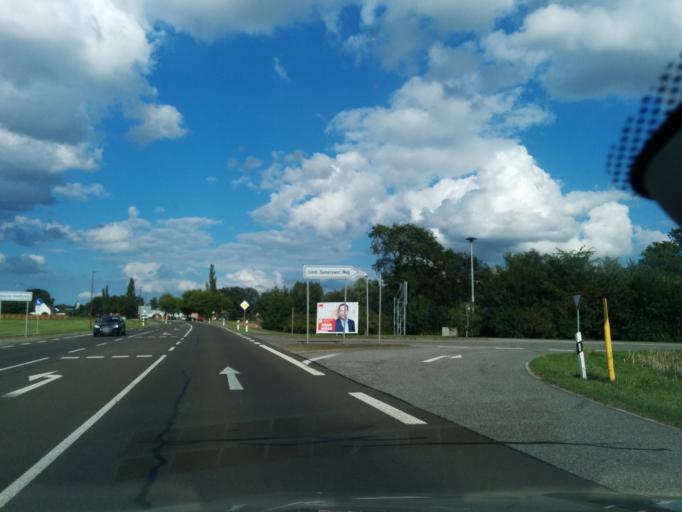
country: DE
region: Mecklenburg-Vorpommern
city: Pasewalk
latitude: 53.4670
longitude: 13.9715
